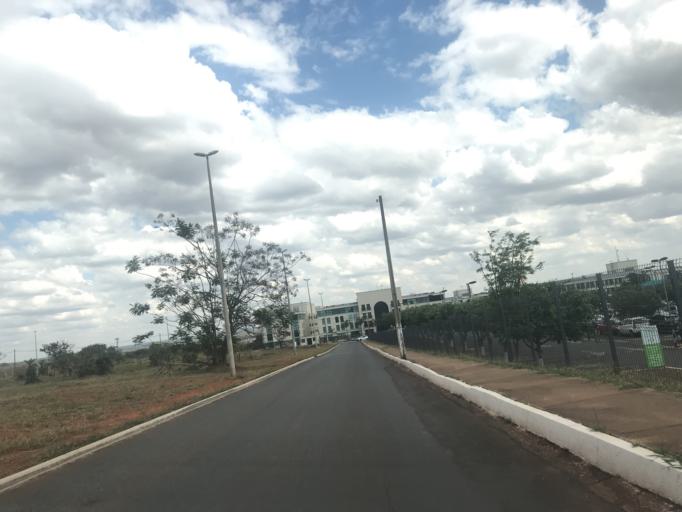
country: BR
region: Federal District
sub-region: Brasilia
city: Brasilia
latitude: -15.8346
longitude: -47.9495
